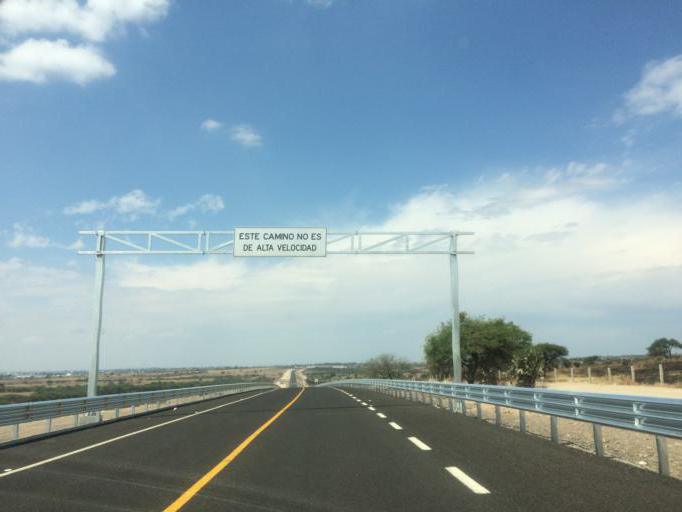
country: MX
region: Guanajuato
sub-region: Silao de la Victoria
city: San Francisco (Banos de Agua Caliente)
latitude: 21.0346
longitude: -101.4804
